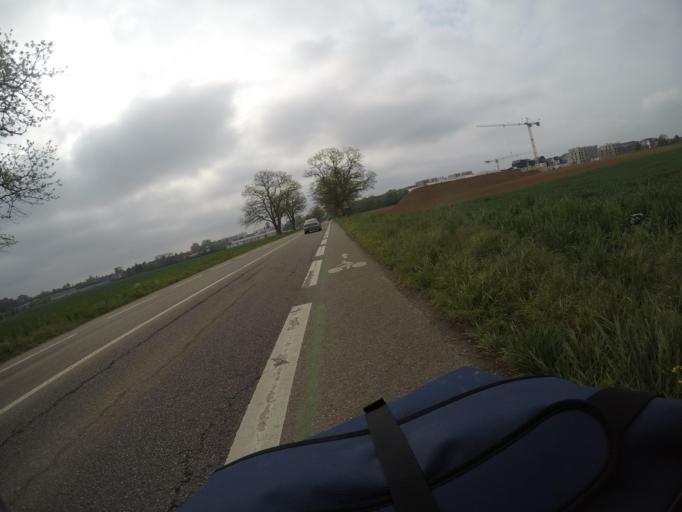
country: FR
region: Alsace
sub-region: Departement du Bas-Rhin
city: Mittelhausbergen
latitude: 48.6079
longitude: 7.7014
